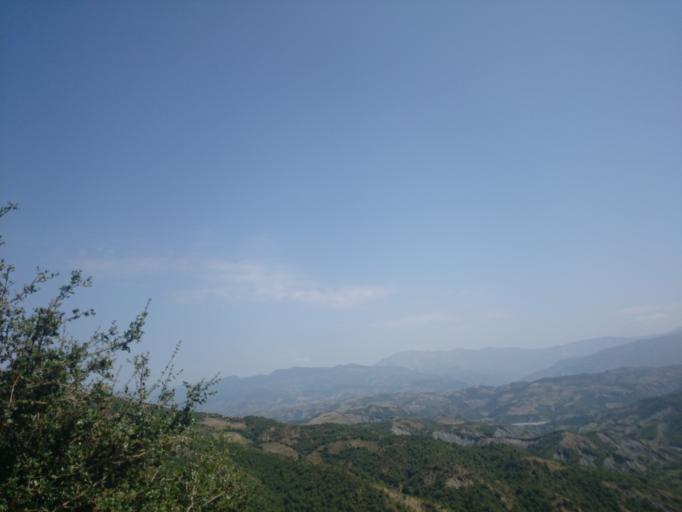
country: AL
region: Elbasan
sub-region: Rrethi i Gramshit
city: Kushove
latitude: 40.7510
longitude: 20.1649
